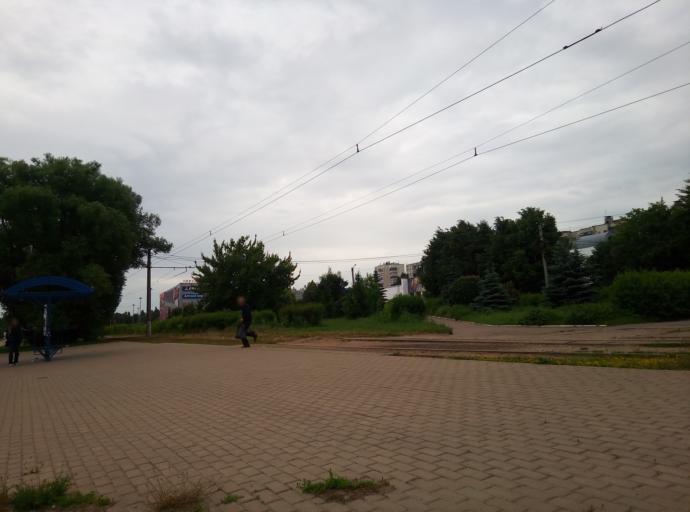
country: RU
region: Kursk
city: Kursk
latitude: 51.7444
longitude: 36.1445
